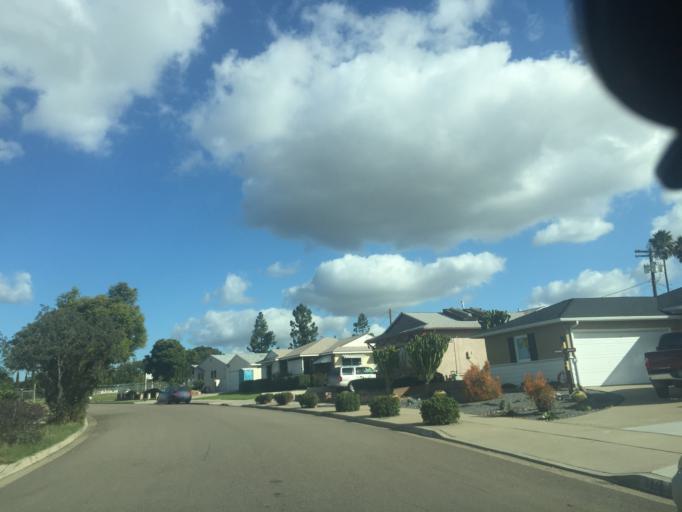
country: US
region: California
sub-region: San Diego County
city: La Mesa
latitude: 32.7920
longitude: -117.0826
